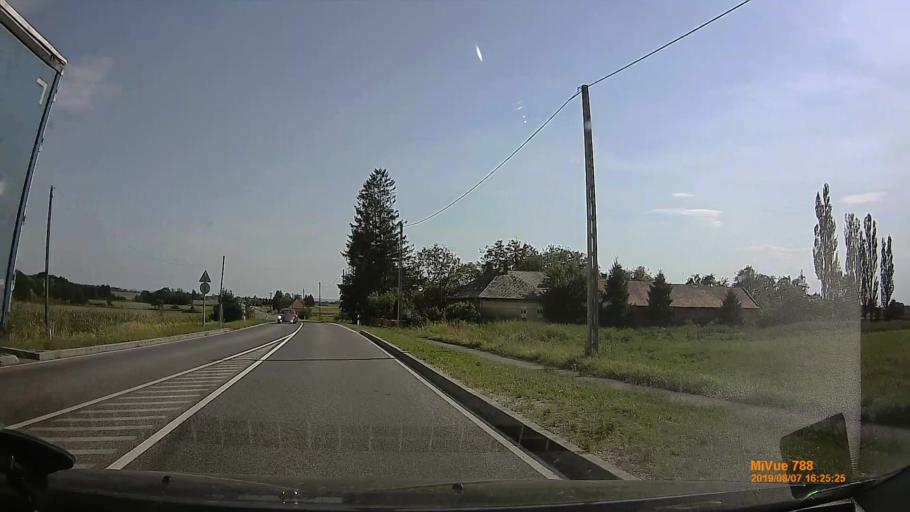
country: HU
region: Zala
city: Lenti
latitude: 46.7228
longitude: 16.5496
